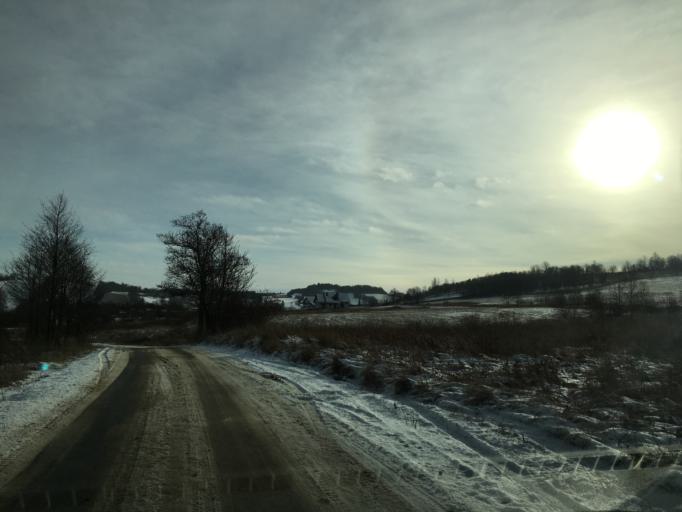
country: PL
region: Lower Silesian Voivodeship
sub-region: Powiat walbrzyski
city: Gluszyca Gorna
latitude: 50.6733
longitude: 16.3661
